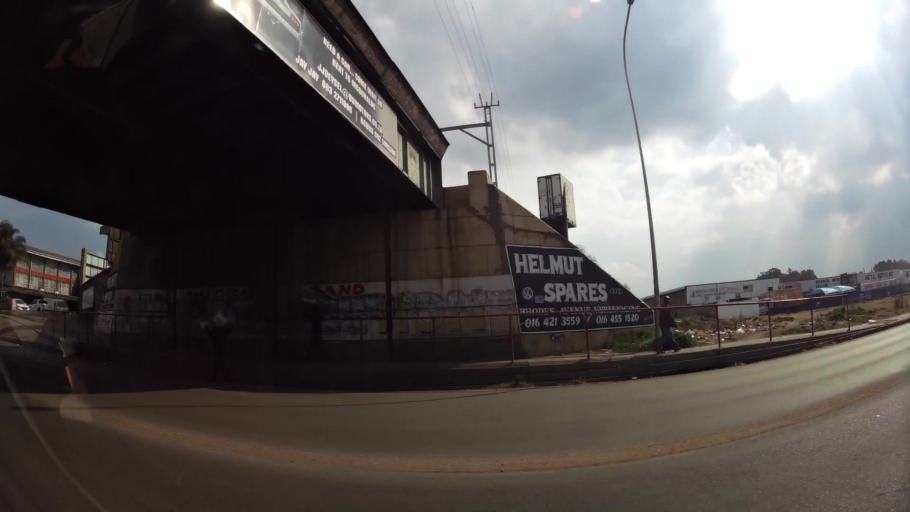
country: ZA
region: Gauteng
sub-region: Sedibeng District Municipality
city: Vereeniging
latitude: -26.6659
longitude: 27.9337
